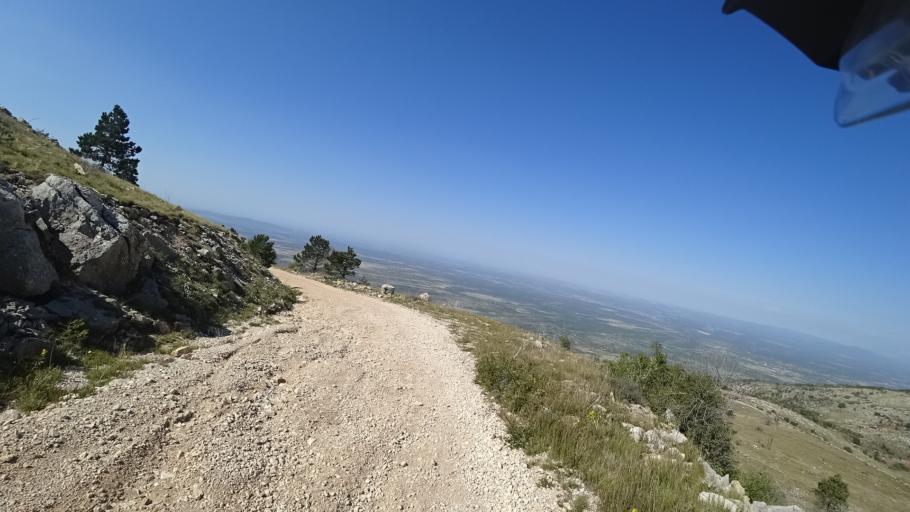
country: HR
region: Sibensko-Kniniska
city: Drnis
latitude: 43.9262
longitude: 16.1662
